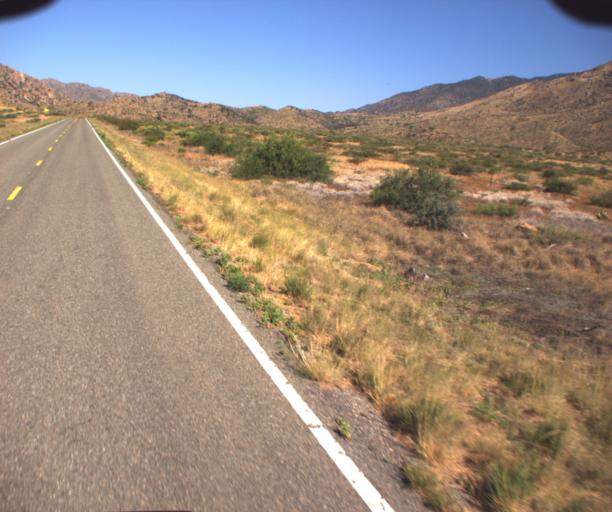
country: US
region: Arizona
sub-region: Graham County
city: Swift Trail Junction
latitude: 32.5606
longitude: -109.7724
